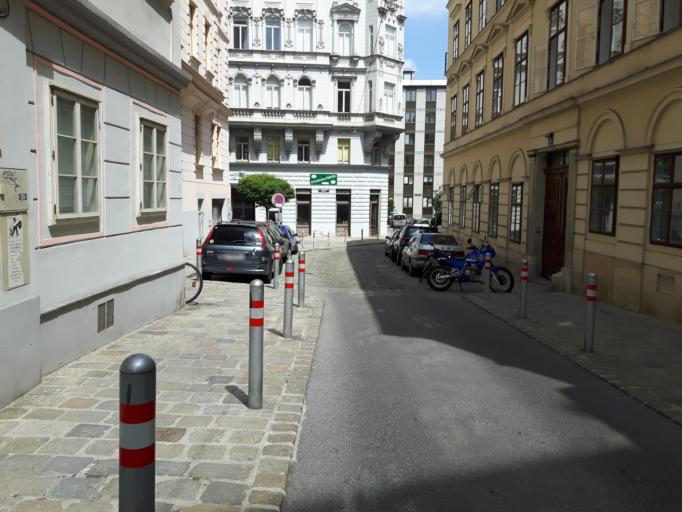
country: AT
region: Vienna
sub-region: Wien Stadt
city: Vienna
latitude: 48.2047
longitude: 16.3549
